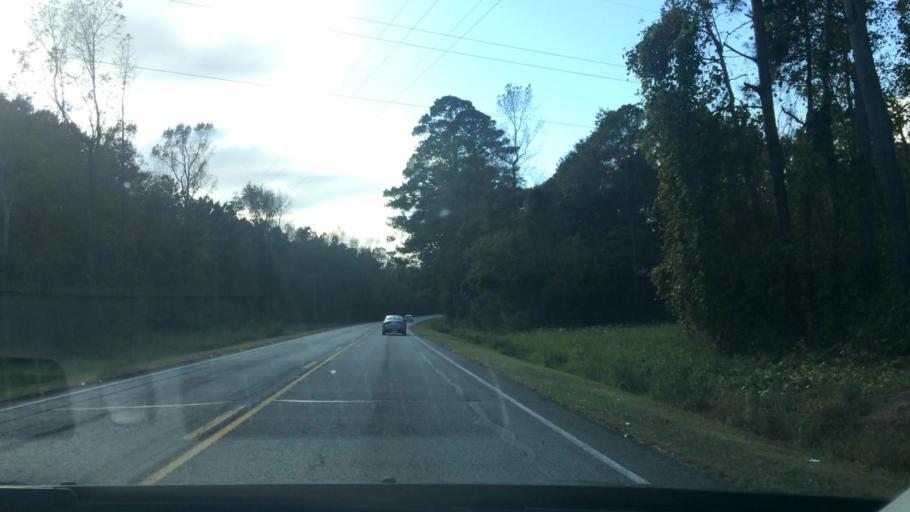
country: US
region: North Carolina
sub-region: Greene County
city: Snow Hill
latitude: 35.4394
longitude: -77.7549
